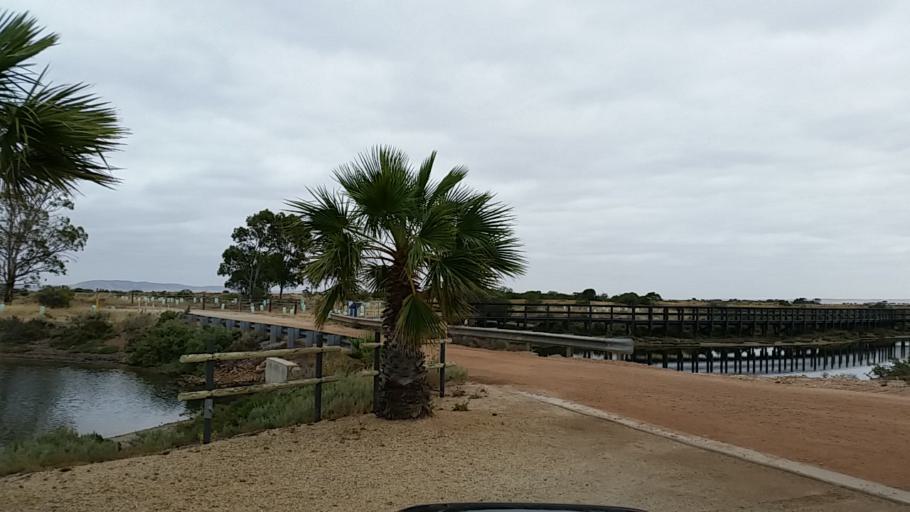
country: AU
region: South Australia
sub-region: Wakefield
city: Balaklava
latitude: -34.1841
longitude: 138.1455
